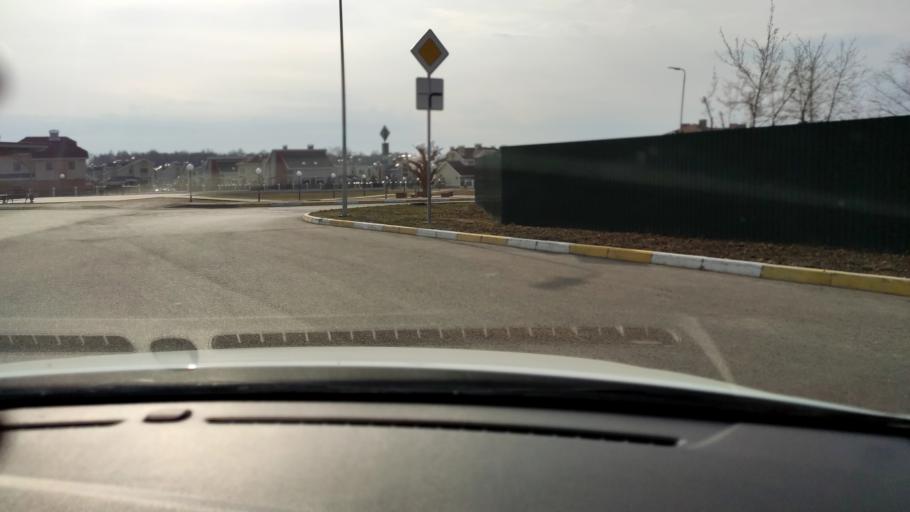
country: RU
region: Tatarstan
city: Stolbishchi
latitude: 55.7137
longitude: 49.2138
